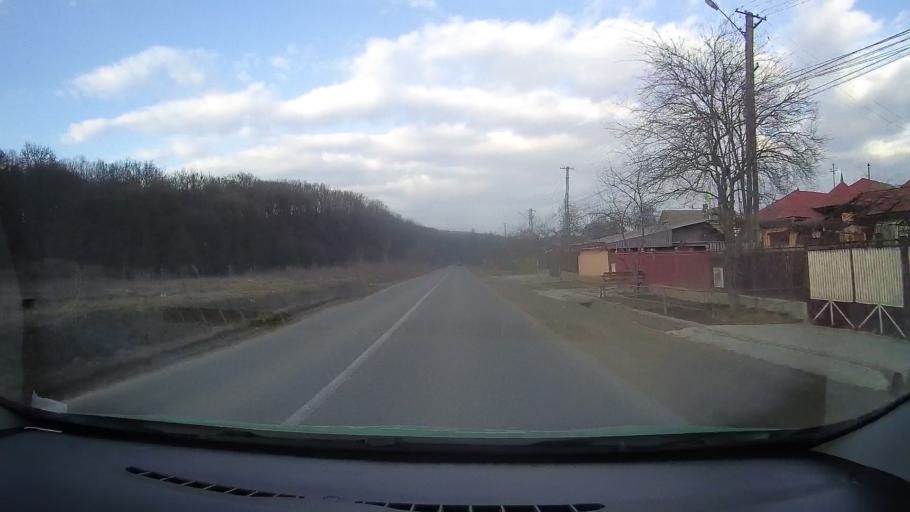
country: RO
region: Dambovita
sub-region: Comuna Gura Ocnitei
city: Gura Ocnitei
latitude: 44.9427
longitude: 25.5829
